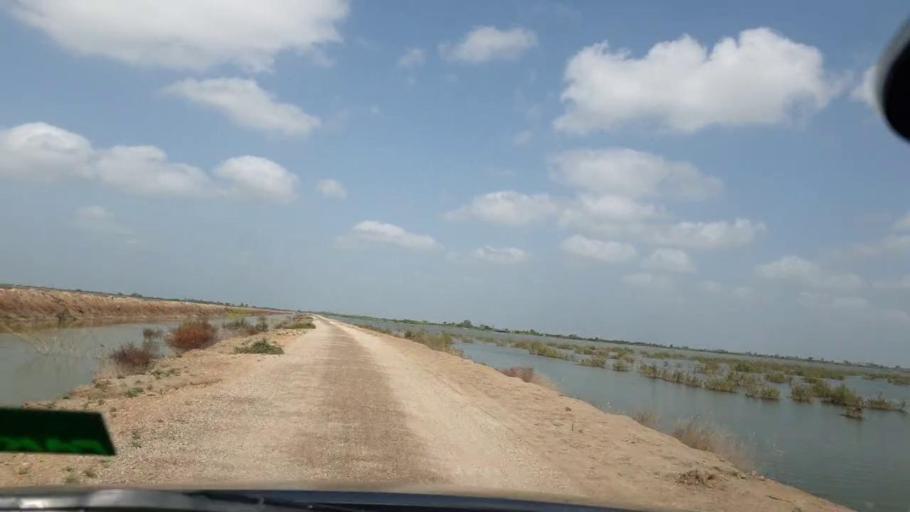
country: PK
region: Sindh
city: Kadhan
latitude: 24.5869
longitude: 69.1394
